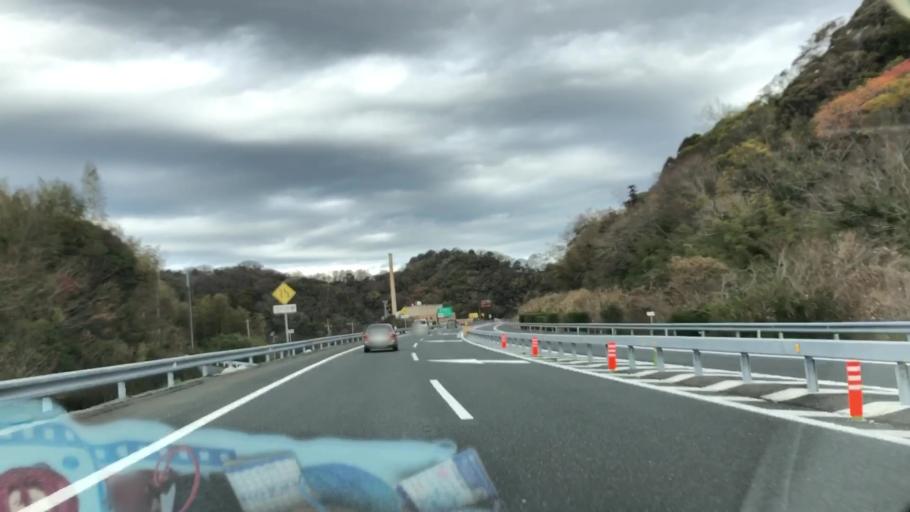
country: JP
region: Chiba
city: Tateyama
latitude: 35.1024
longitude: 139.8545
